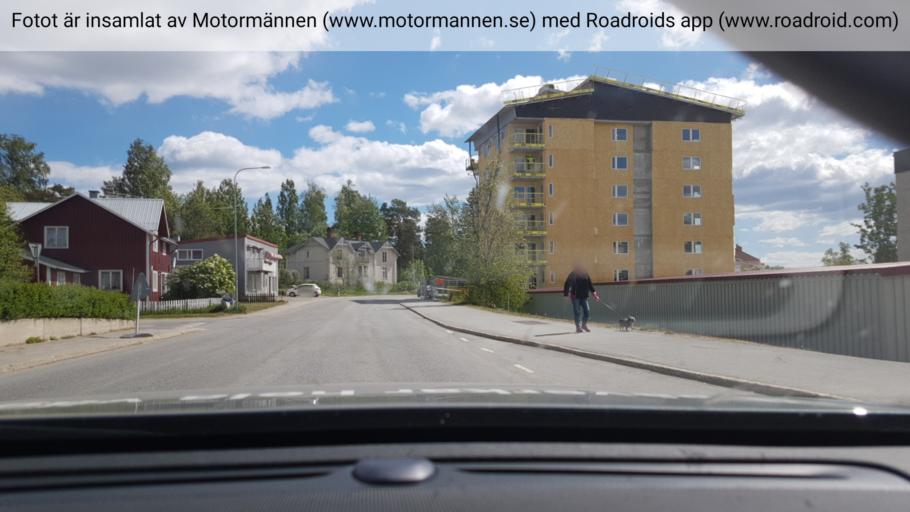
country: SE
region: Vaesterbotten
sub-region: Nordmalings Kommun
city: Nordmaling
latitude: 63.5725
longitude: 19.4935
